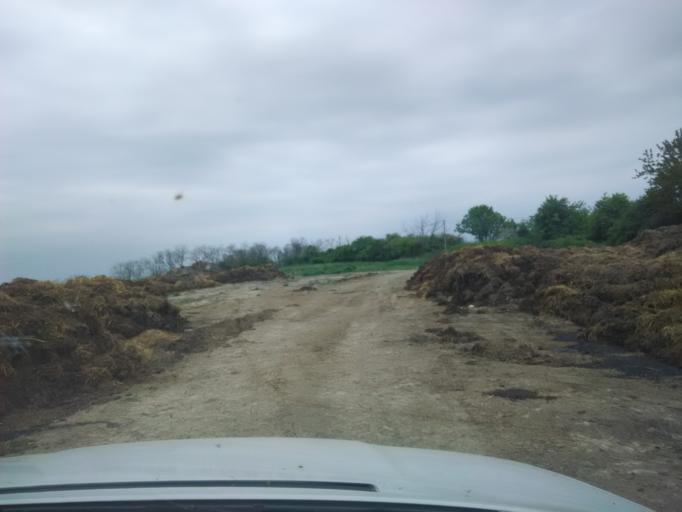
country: SK
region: Nitriansky
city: Levice
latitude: 48.2847
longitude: 18.7123
